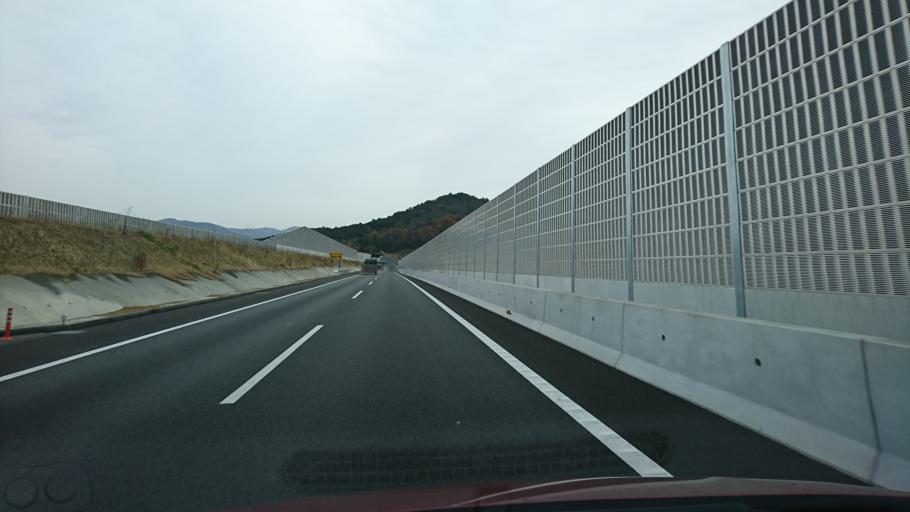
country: JP
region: Hyogo
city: Kawanishi
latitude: 34.8892
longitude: 135.3696
